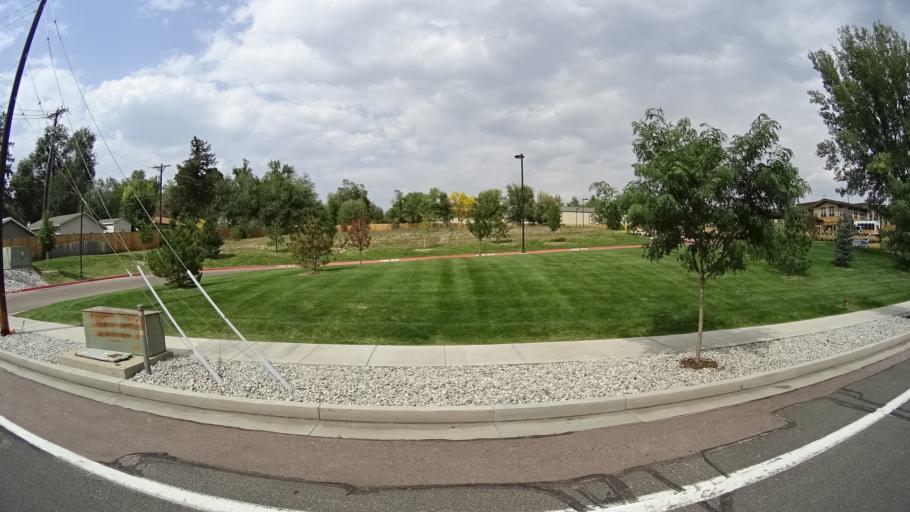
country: US
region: Colorado
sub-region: El Paso County
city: Colorado Springs
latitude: 38.8450
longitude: -104.7846
